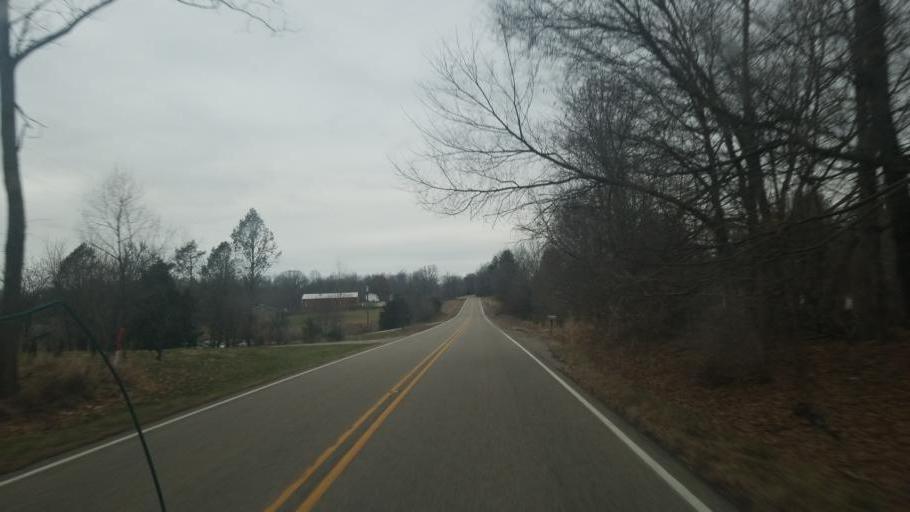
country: US
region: Indiana
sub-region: Owen County
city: Spencer
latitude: 39.3537
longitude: -86.9326
